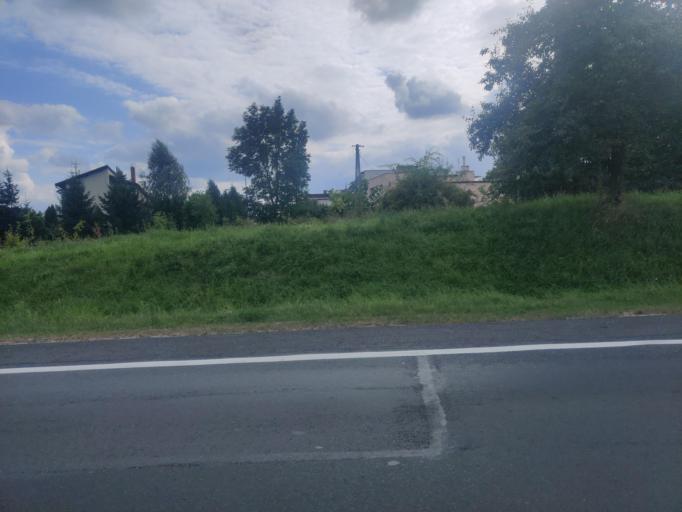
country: PL
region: Greater Poland Voivodeship
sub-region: Konin
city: Konin
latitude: 52.2000
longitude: 18.2872
